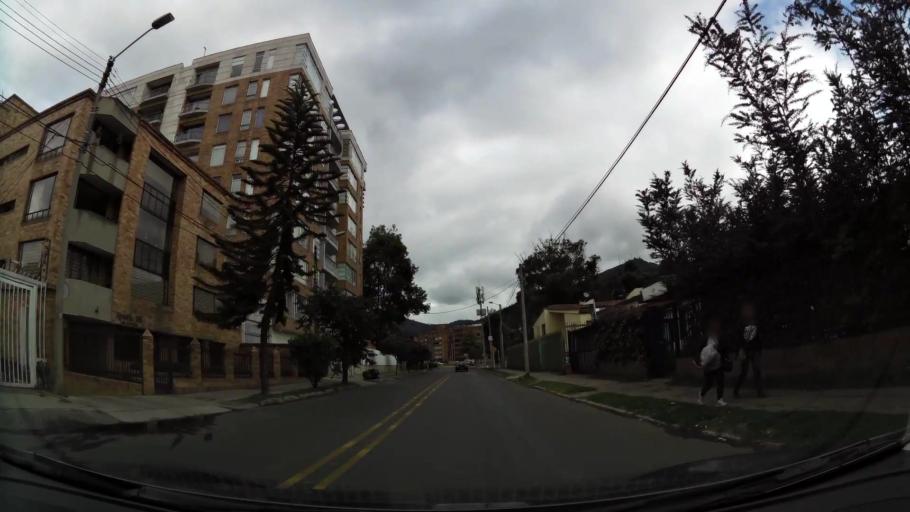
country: CO
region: Bogota D.C.
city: Barrio San Luis
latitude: 4.6828
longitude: -74.0542
